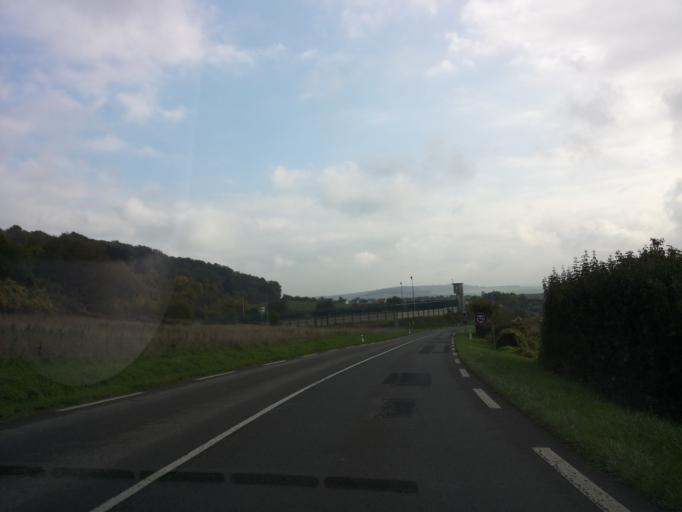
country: FR
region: Lorraine
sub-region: Departement de la Meuse
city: Montmedy
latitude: 49.5249
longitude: 5.3651
